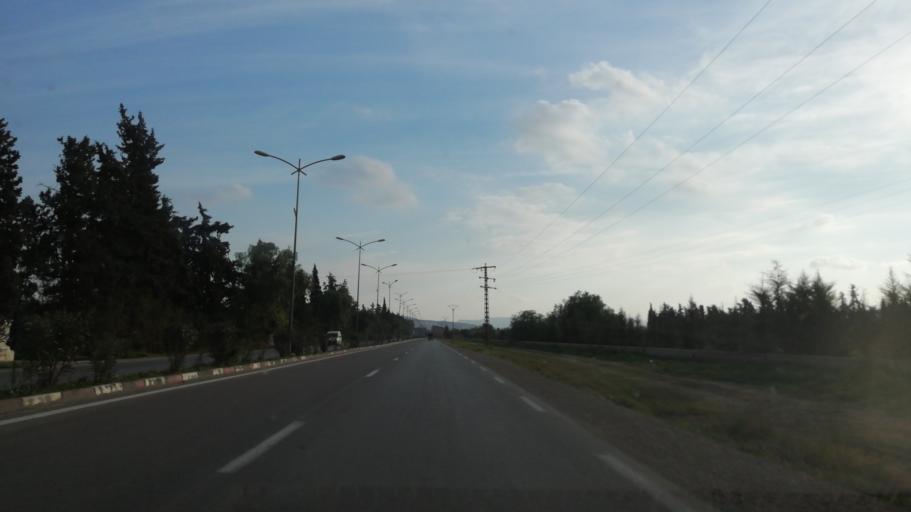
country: DZ
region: Mascara
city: Mascara
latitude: 35.6053
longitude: 0.0634
